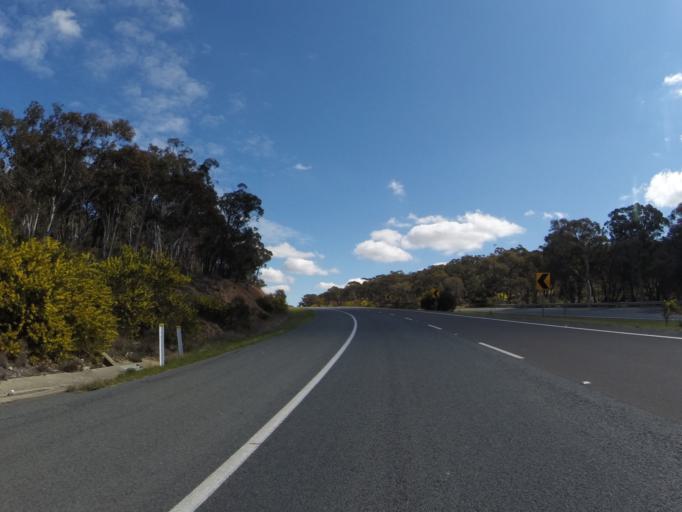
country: AU
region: New South Wales
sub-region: Goulburn Mulwaree
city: Goulburn
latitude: -34.7419
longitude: 149.7625
